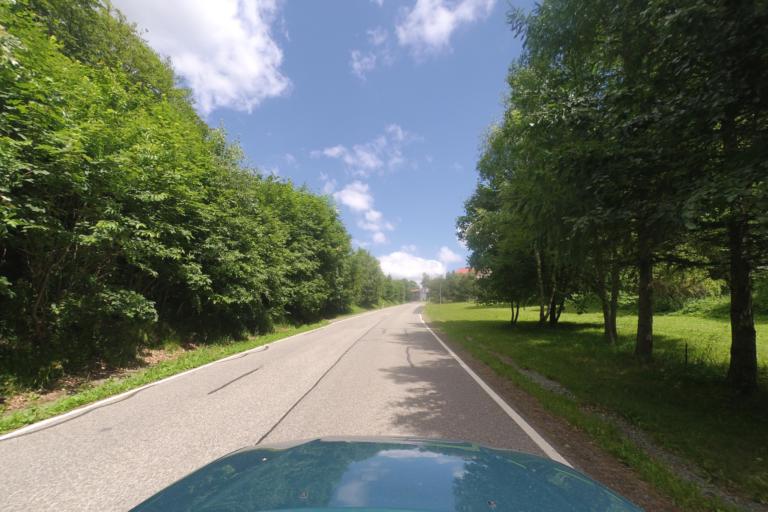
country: PL
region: Lower Silesian Voivodeship
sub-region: Powiat klodzki
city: Lewin Klodzki
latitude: 50.3530
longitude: 16.2444
